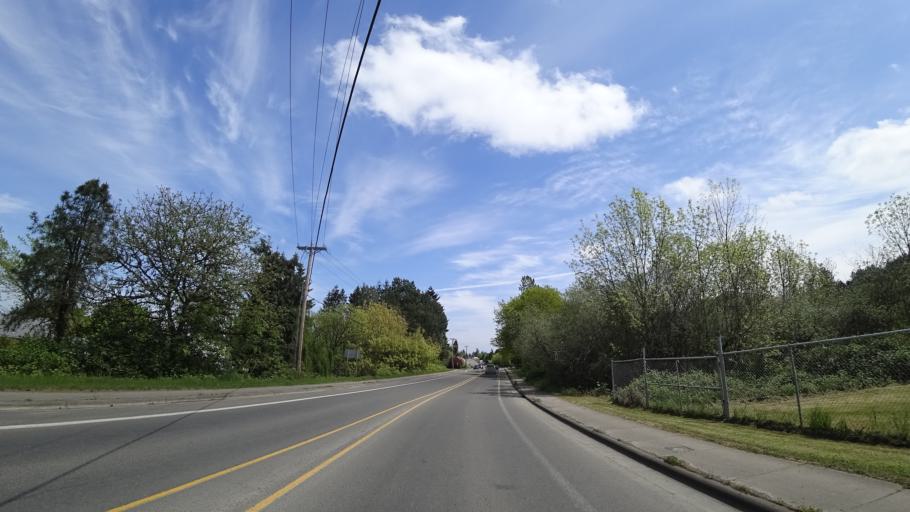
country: US
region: Oregon
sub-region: Washington County
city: Aloha
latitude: 45.4676
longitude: -122.8907
